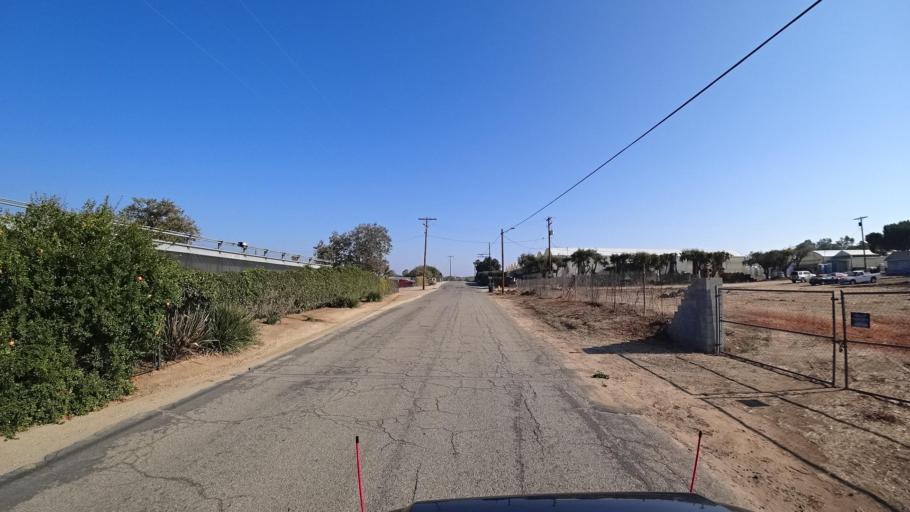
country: US
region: California
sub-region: San Diego County
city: Bonsall
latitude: 33.3241
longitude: -117.2601
